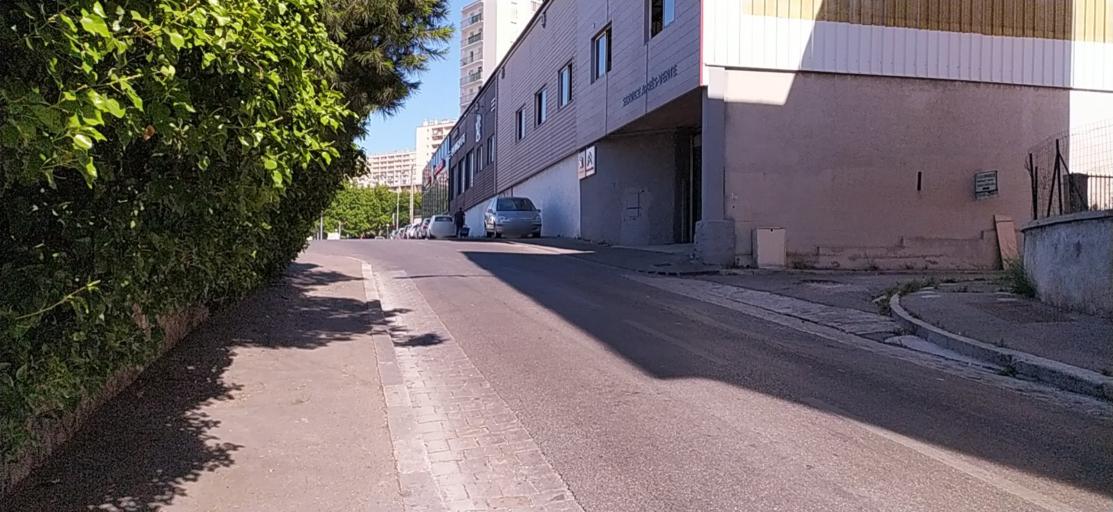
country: FR
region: Provence-Alpes-Cote d'Azur
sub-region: Departement des Bouches-du-Rhone
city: Marseille 14
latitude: 43.3422
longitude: 5.3613
